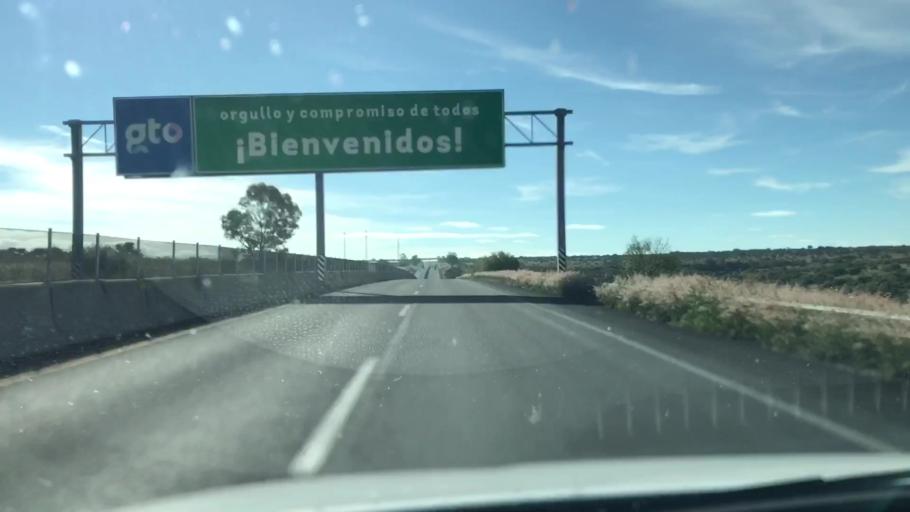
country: MX
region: Guanajuato
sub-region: Leon
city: Rizos de la Joya (Rizos del Saucillo)
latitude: 21.1193
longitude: -101.8066
